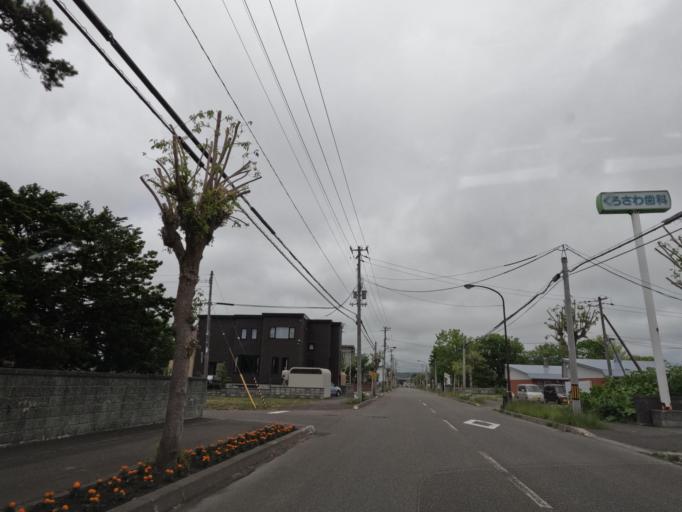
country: JP
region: Hokkaido
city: Tobetsu
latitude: 43.2273
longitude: 141.5172
